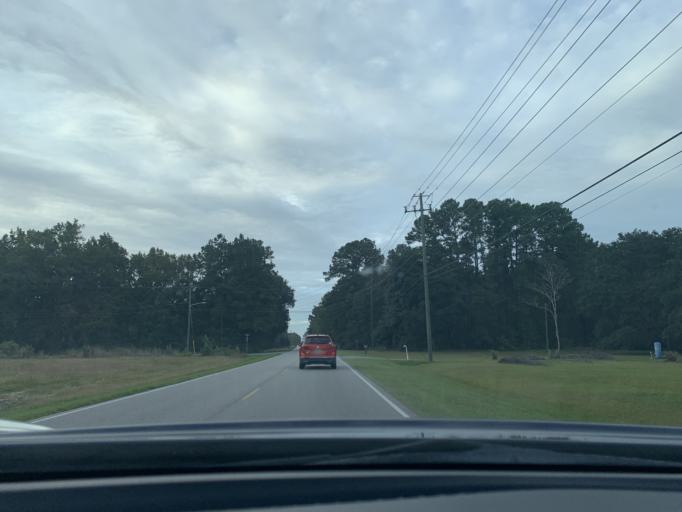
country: US
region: Georgia
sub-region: Chatham County
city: Pooler
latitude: 32.0597
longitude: -81.2701
